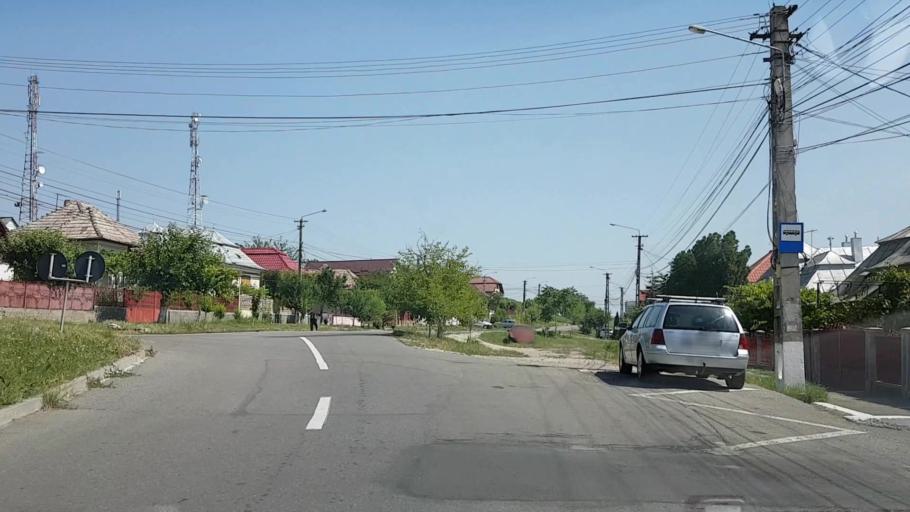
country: RO
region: Cluj
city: Turda
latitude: 46.5795
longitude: 23.7947
